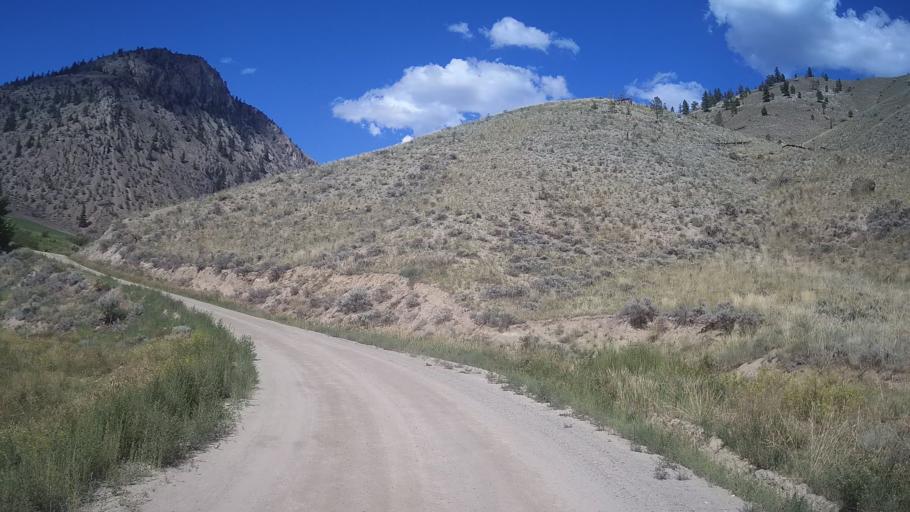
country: CA
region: British Columbia
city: Lillooet
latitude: 51.1919
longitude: -122.1185
